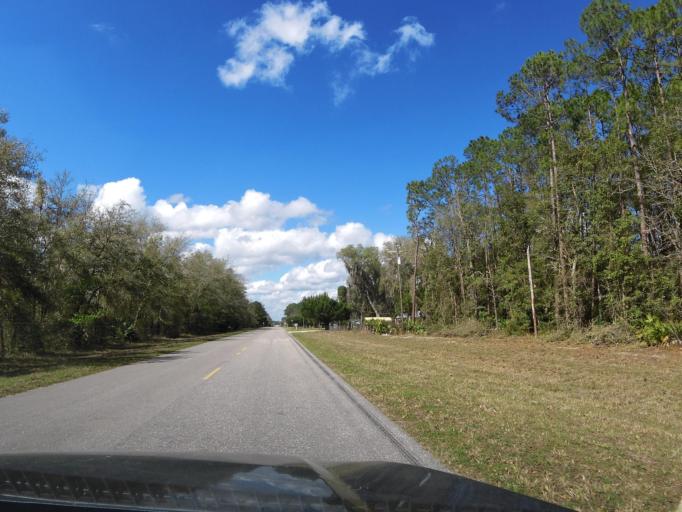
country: US
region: Florida
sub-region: Clay County
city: Green Cove Springs
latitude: 29.8680
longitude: -81.6666
